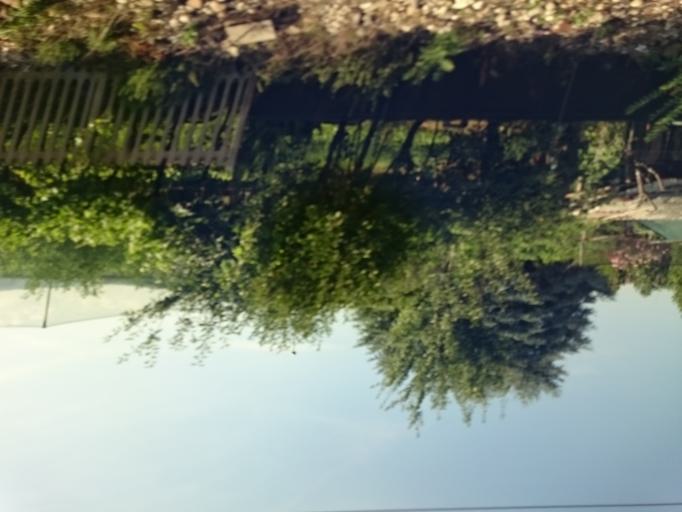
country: IT
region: Veneto
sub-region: Provincia di Verona
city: Ospedaletto
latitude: 45.5079
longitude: 10.8384
